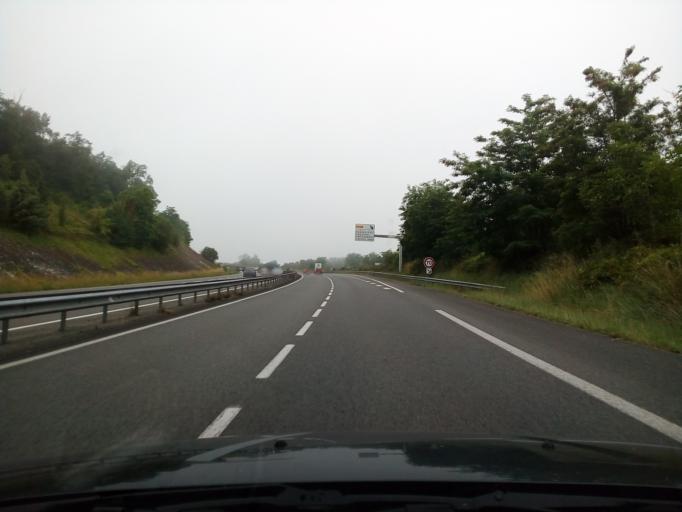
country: FR
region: Poitou-Charentes
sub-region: Departement de la Charente
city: Jarnac
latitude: 45.6683
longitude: -0.1842
